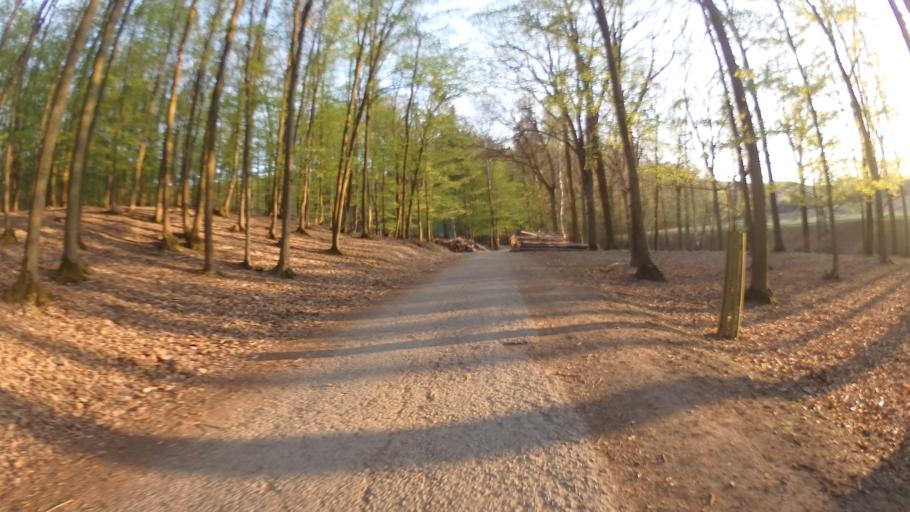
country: CZ
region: South Moravian
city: Troubsko
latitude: 49.2057
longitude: 16.5231
